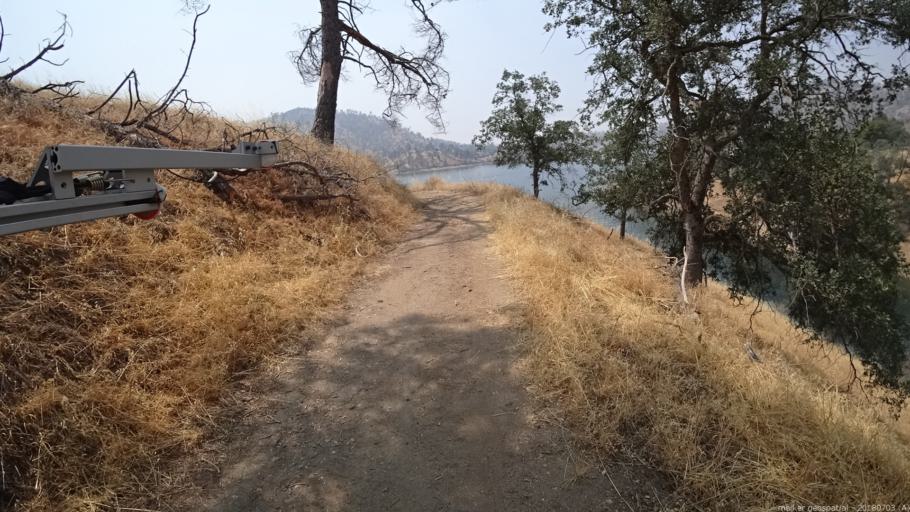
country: US
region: California
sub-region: Fresno County
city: Auberry
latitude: 37.0469
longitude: -119.6510
